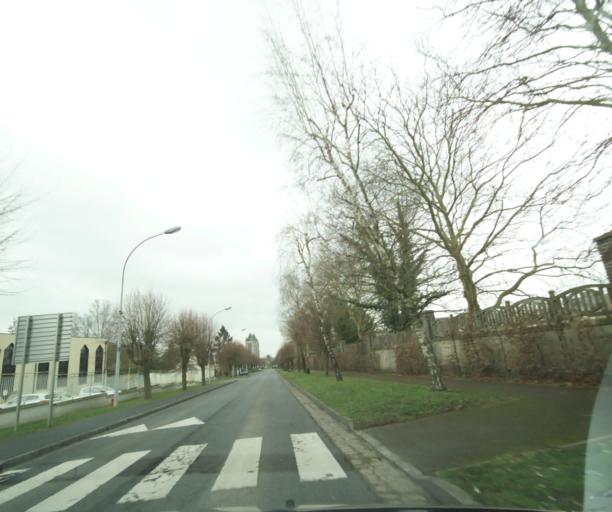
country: FR
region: Picardie
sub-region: Departement de l'Oise
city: Noyon
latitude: 49.5882
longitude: 3.0021
